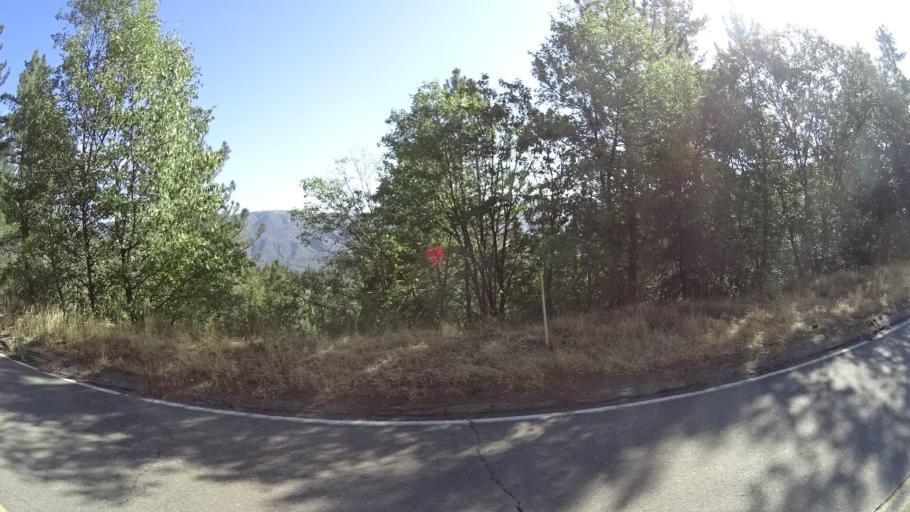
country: US
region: California
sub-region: Riverside County
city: Aguanga
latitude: 33.2874
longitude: -116.7969
